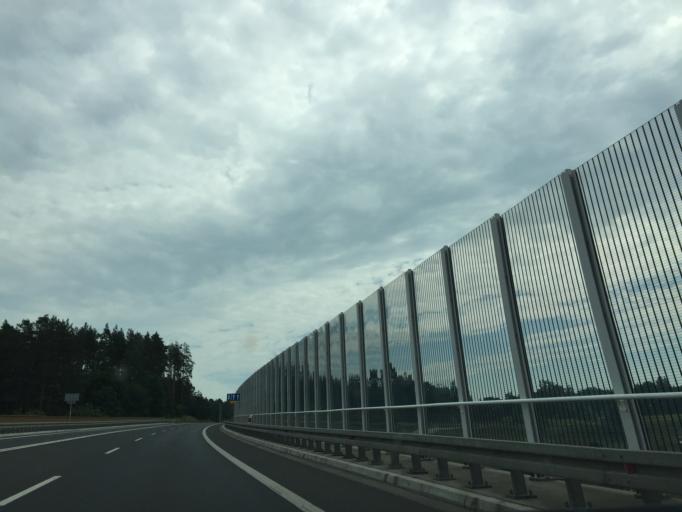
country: PL
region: Warmian-Masurian Voivodeship
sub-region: Powiat mragowski
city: Mragowo
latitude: 53.8857
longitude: 21.3164
